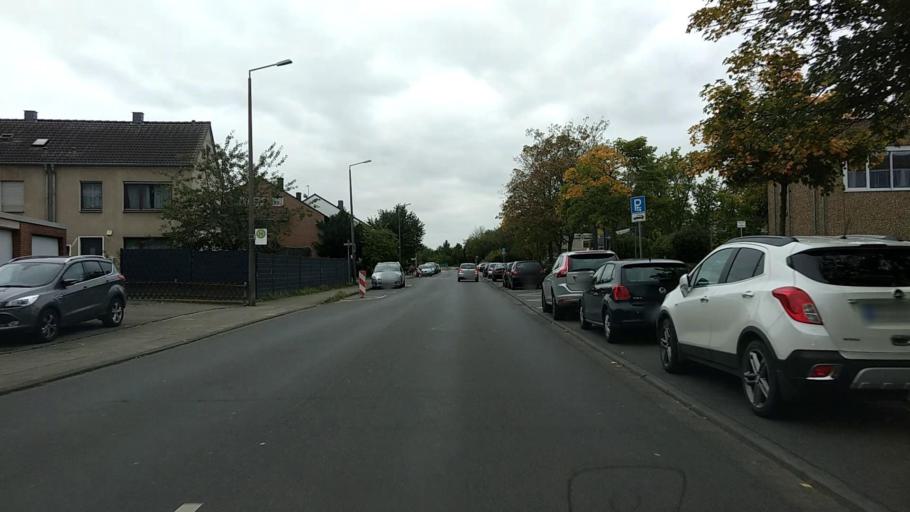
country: DE
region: North Rhine-Westphalia
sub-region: Regierungsbezirk Koln
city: Bergheim
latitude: 50.9496
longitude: 6.6338
